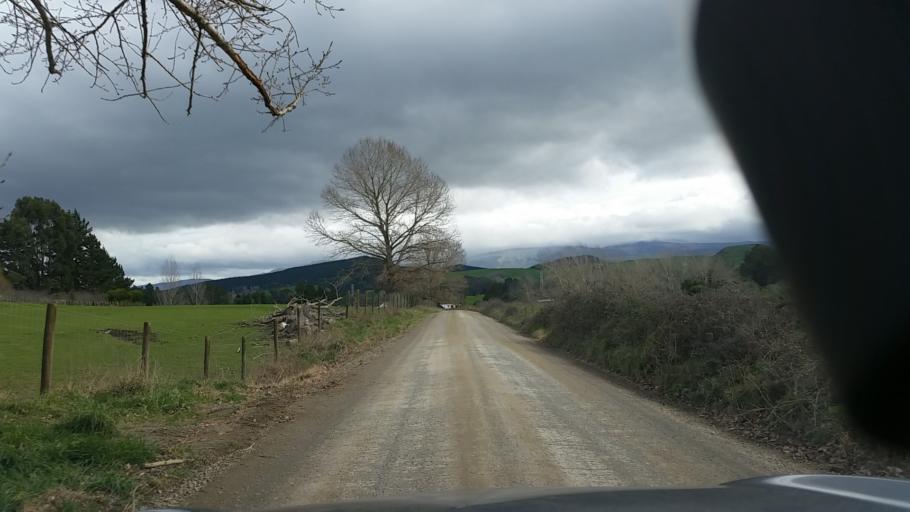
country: NZ
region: Hawke's Bay
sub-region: Napier City
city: Napier
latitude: -39.1883
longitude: 176.9088
